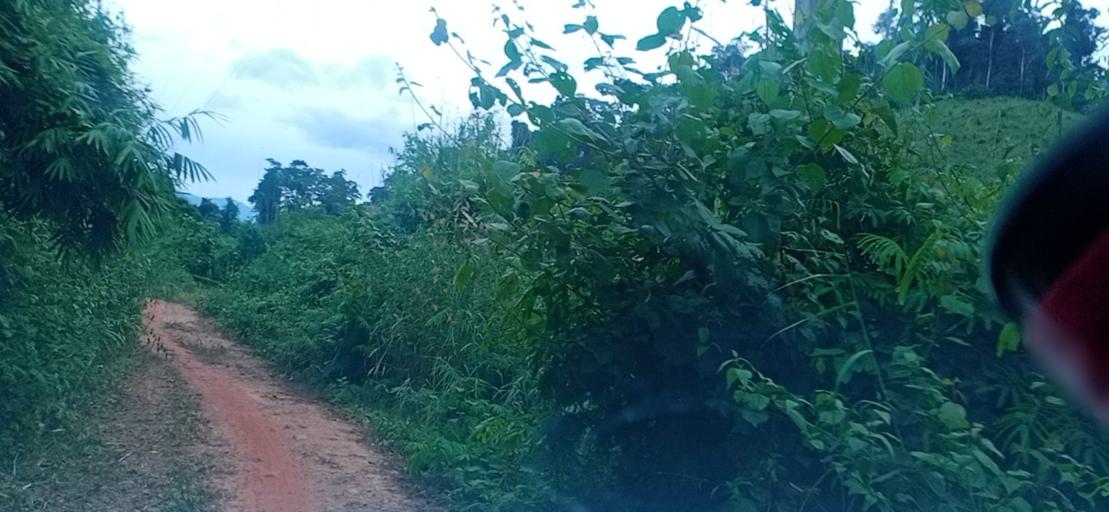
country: TH
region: Changwat Bueng Kan
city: Pak Khat
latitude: 18.5607
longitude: 103.2610
